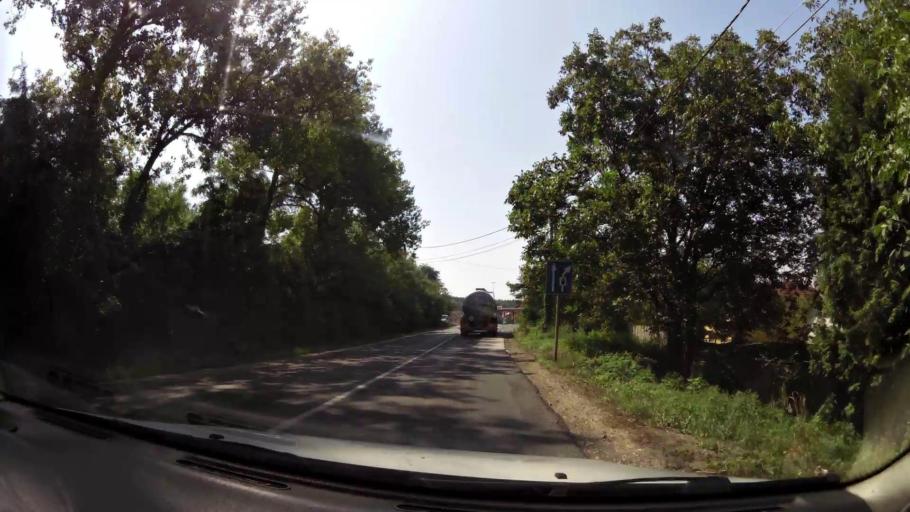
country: HU
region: Pest
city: Mende
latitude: 47.4337
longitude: 19.4625
